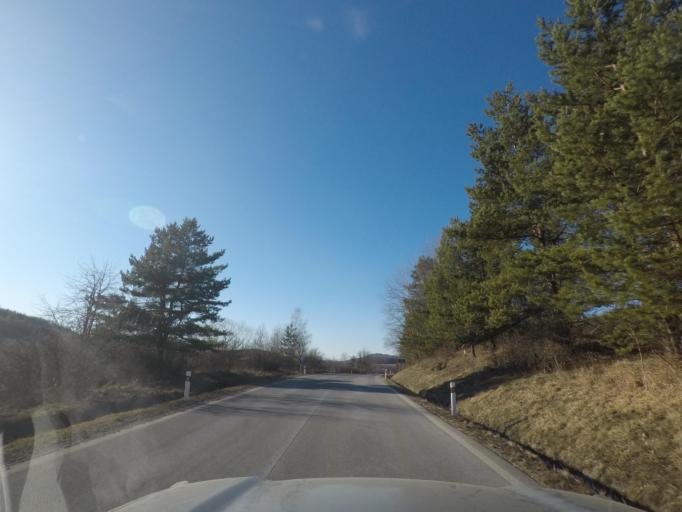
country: SK
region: Presovsky
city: Medzilaborce
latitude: 49.2782
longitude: 21.8579
